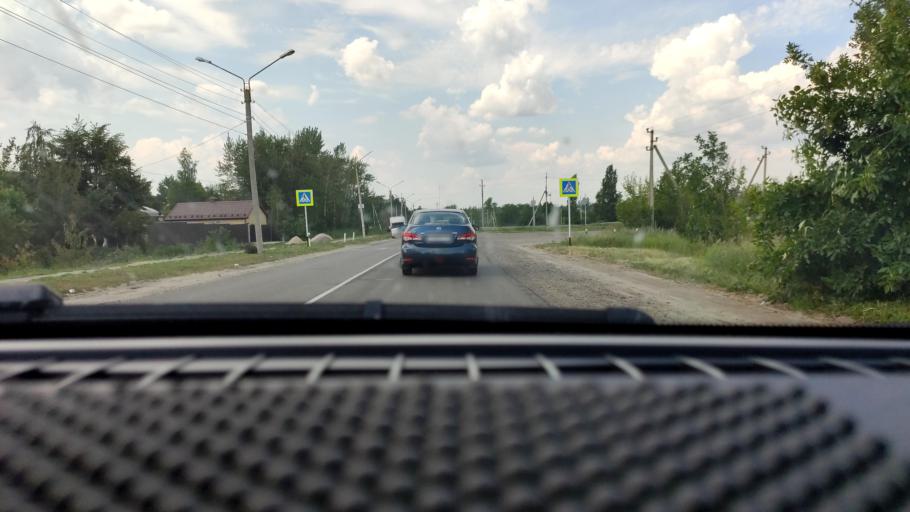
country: RU
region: Voronezj
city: Novaya Usman'
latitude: 51.6567
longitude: 39.4382
